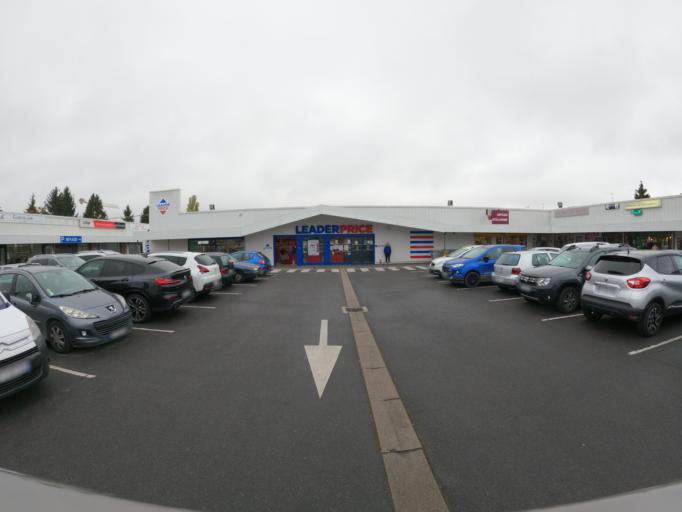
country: FR
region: Ile-de-France
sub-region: Departement du Val-de-Marne
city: Chennevieres-sur-Marne
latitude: 48.7918
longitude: 2.5355
